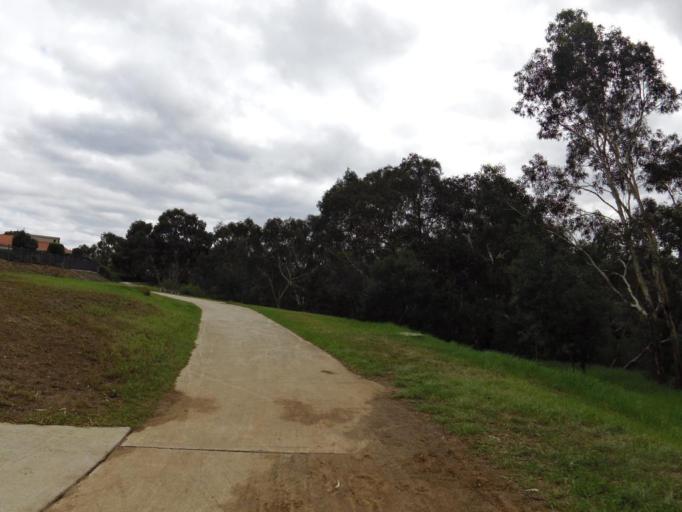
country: AU
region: Victoria
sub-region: Wyndham
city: Werribee
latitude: -37.8991
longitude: 144.6564
